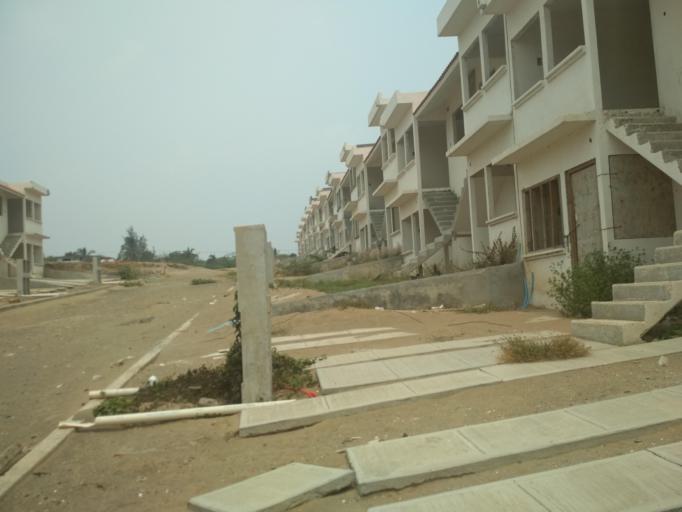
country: MX
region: Veracruz
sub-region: Veracruz
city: Rio Medio [Granja]
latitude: 19.2099
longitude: -96.2119
